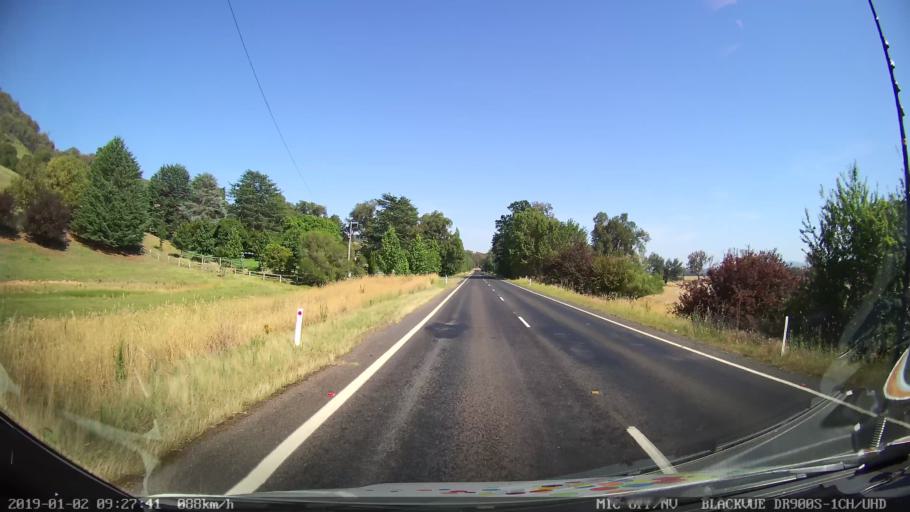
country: AU
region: New South Wales
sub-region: Tumut Shire
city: Tumut
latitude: -35.3592
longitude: 148.2554
